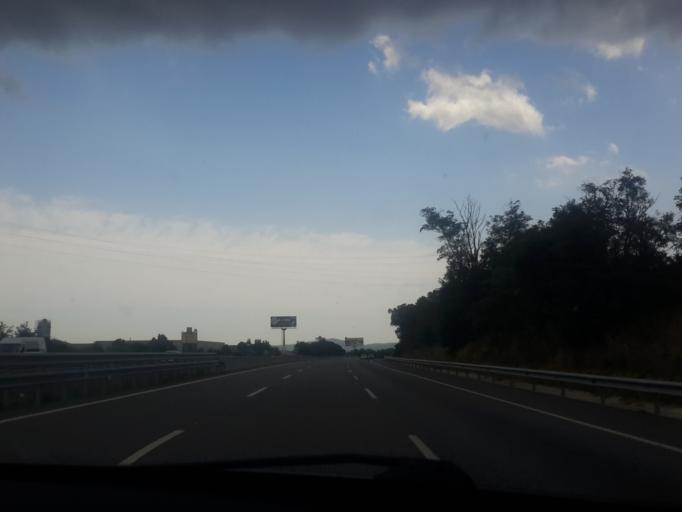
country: ES
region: Catalonia
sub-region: Provincia de Girona
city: Sils
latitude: 41.8122
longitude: 2.7477
